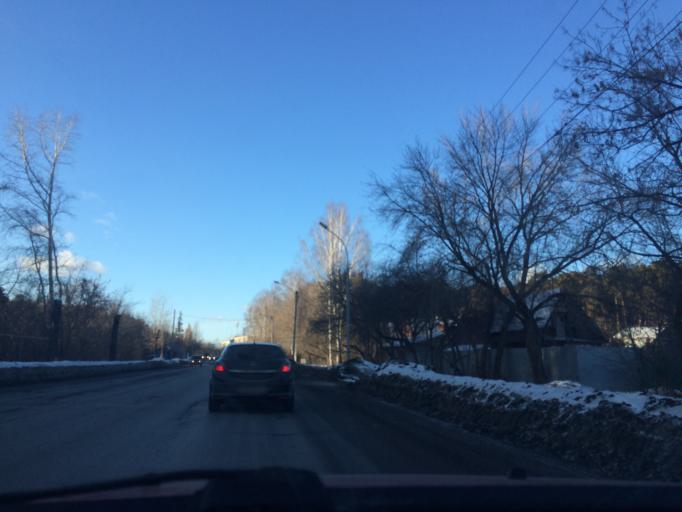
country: RU
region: Sverdlovsk
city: Istok
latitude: 56.7761
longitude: 60.8029
